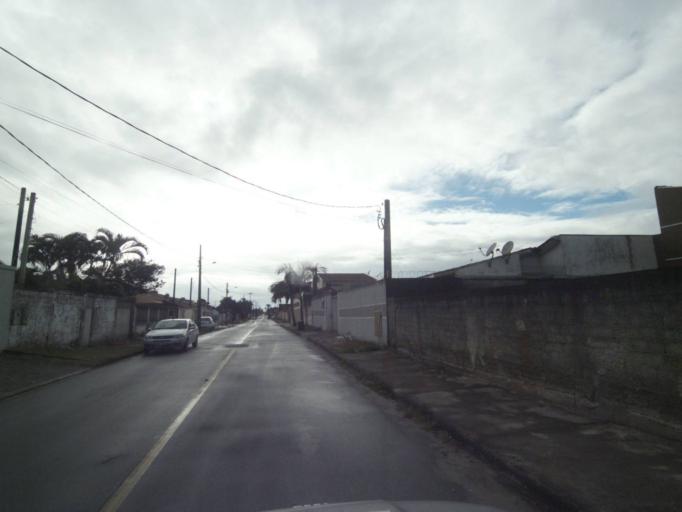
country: BR
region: Parana
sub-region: Paranagua
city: Paranagua
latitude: -25.5661
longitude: -48.5712
